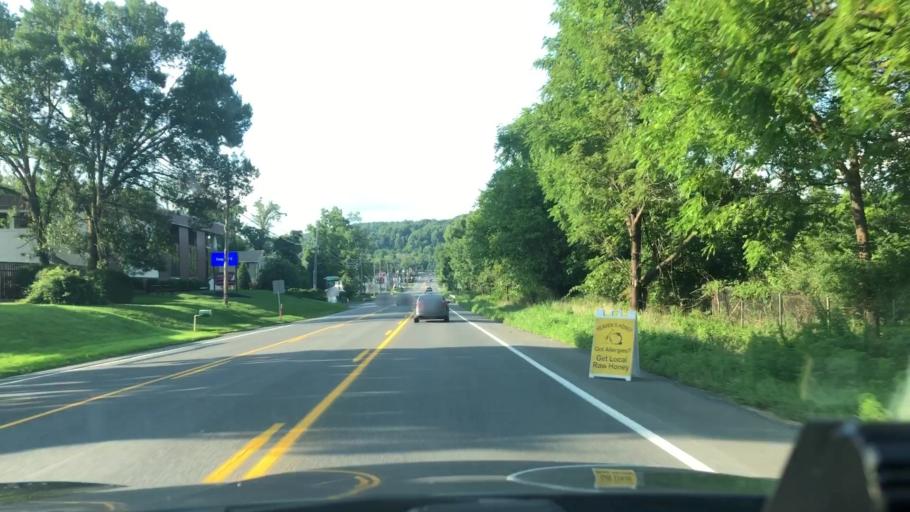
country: US
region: Pennsylvania
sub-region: Lehigh County
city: Fountain Hill
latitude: 40.5786
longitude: -75.3889
